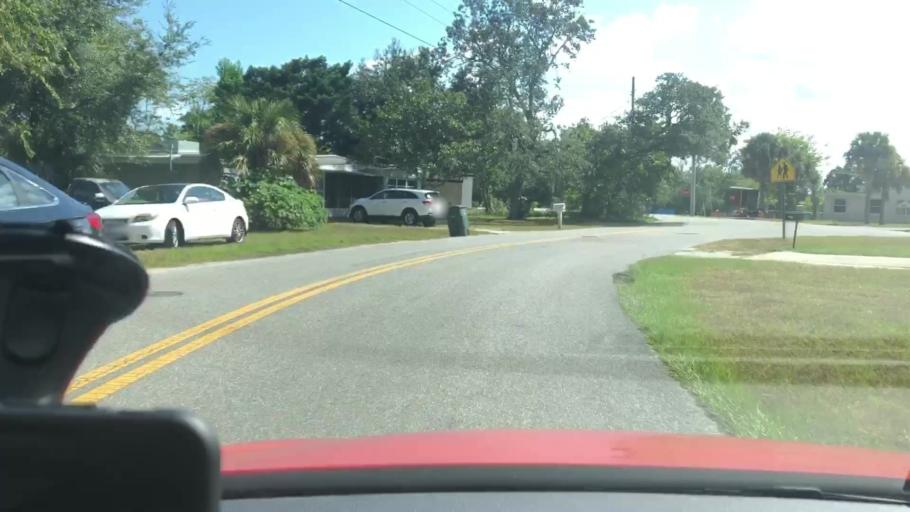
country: US
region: Florida
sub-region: Volusia County
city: Daytona Beach
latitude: 29.2079
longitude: -81.0556
